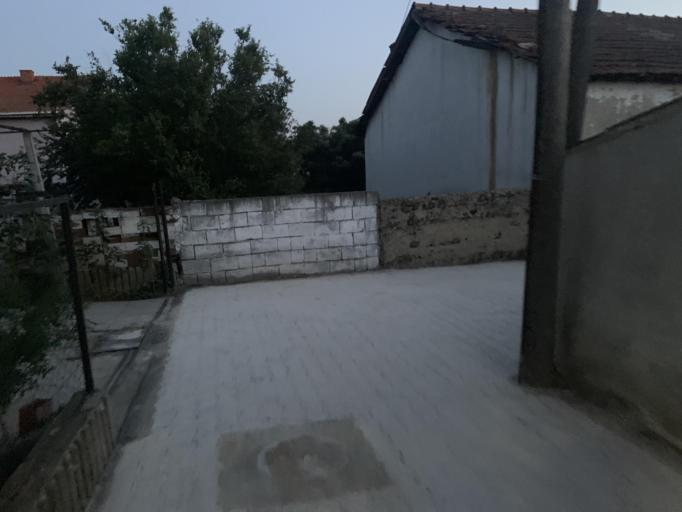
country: MK
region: Bogdanci
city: Bogdanci
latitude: 41.2003
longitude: 22.5730
